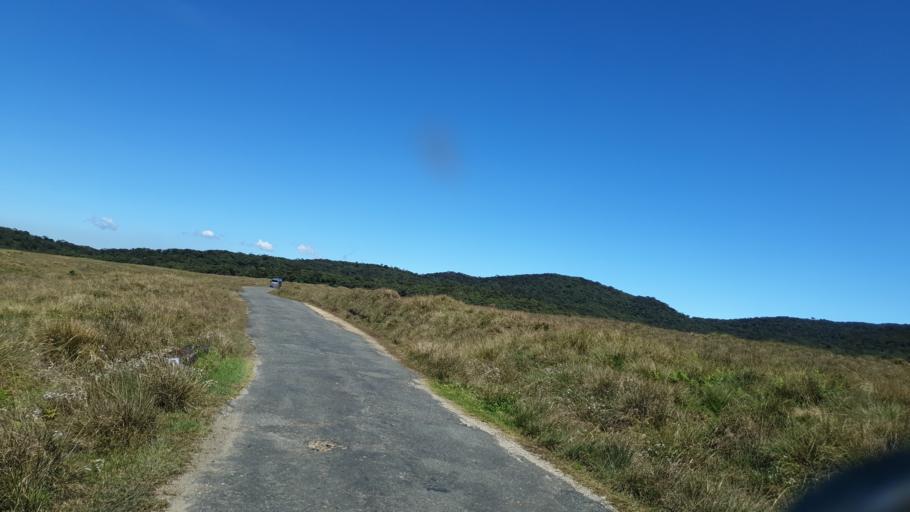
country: LK
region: Central
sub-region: Nuwara Eliya District
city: Nuwara Eliya
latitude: 6.8211
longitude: 80.8060
